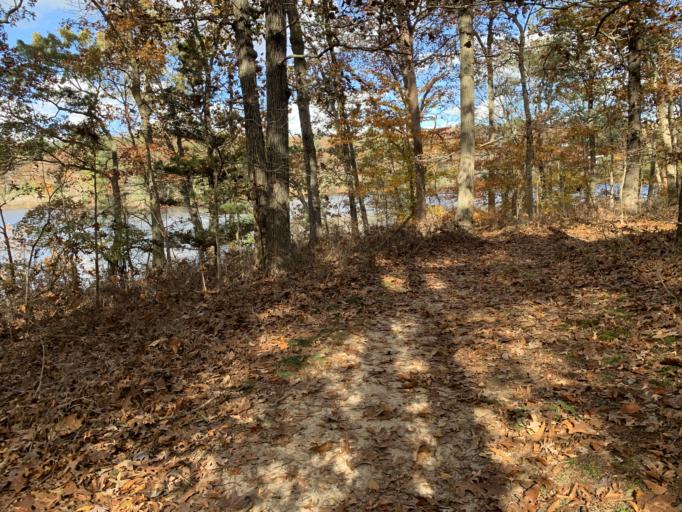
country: US
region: Delaware
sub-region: Kent County
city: Riverview
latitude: 38.9813
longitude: -75.5341
